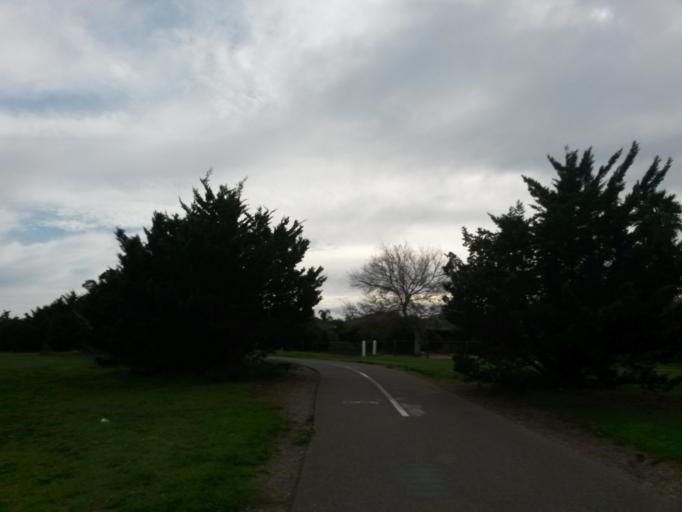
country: AU
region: South Australia
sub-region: Onkaparinga
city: Moana
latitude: -35.1971
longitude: 138.4877
